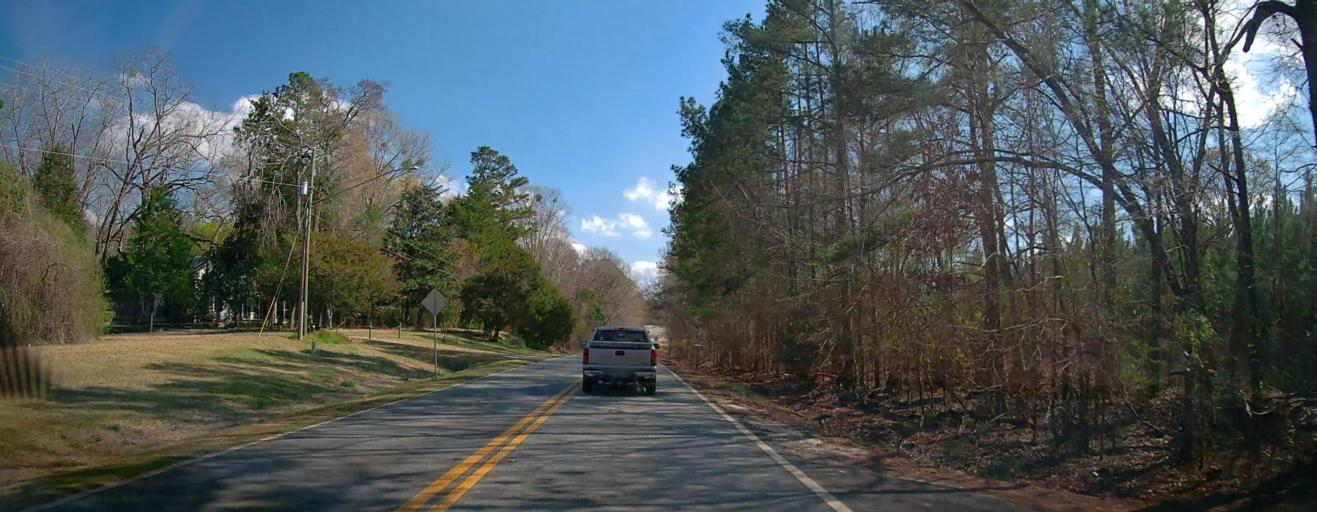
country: US
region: Georgia
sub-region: Twiggs County
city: Jeffersonville
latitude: 32.6991
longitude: -83.3490
